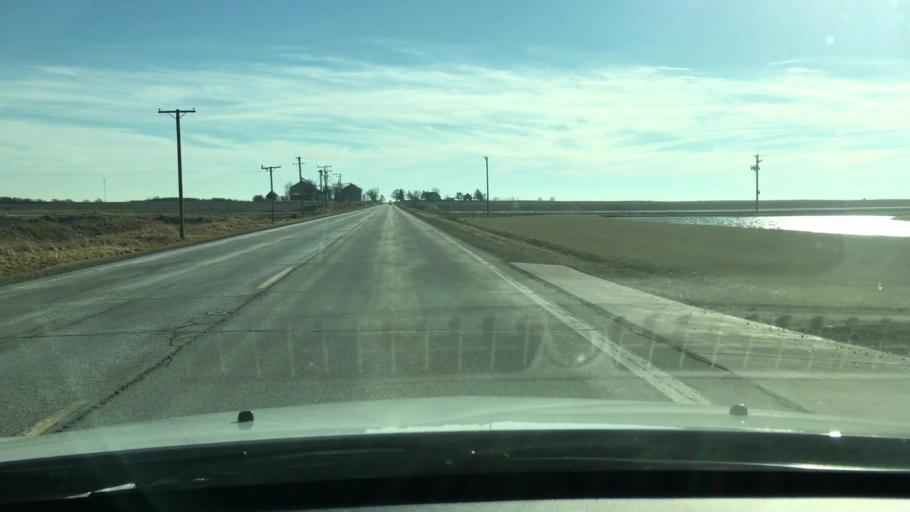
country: US
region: Illinois
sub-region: LaSalle County
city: Mendota
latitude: 41.6002
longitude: -89.1286
